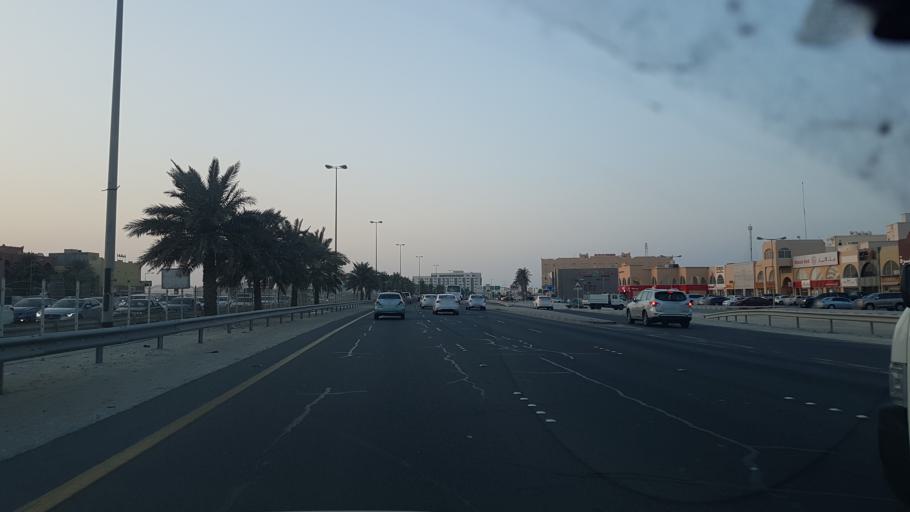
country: BH
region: Northern
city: Ar Rifa'
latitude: 26.1425
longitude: 50.5795
